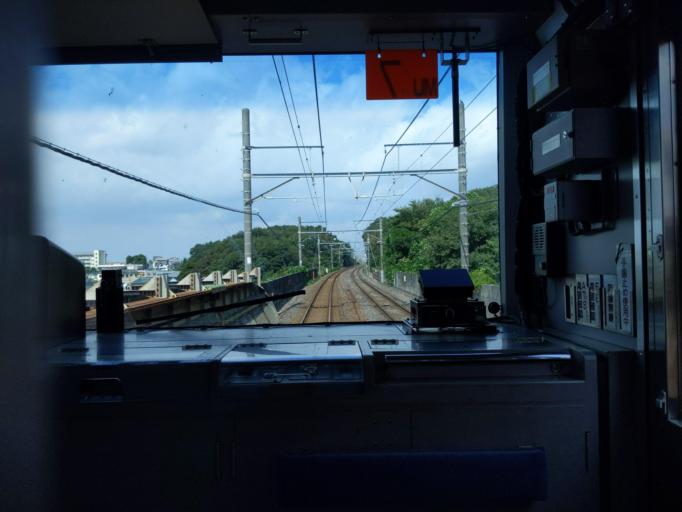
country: JP
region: Chiba
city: Matsudo
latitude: 35.7725
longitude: 139.9432
